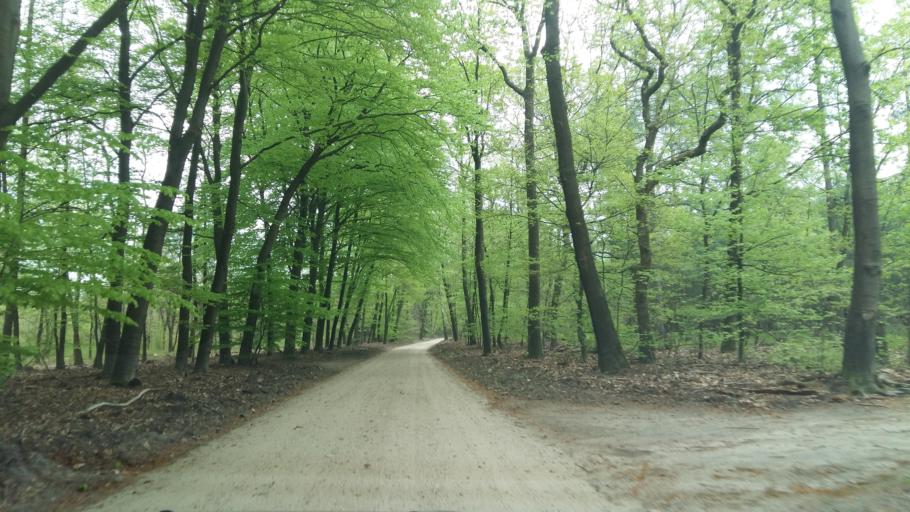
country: NL
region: Gelderland
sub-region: Gemeente Putten
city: Putten
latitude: 52.2611
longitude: 5.6437
